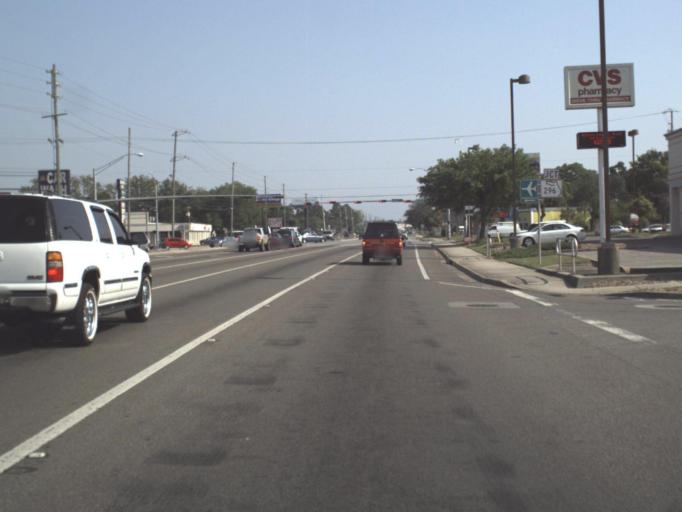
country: US
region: Florida
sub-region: Escambia County
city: Brent
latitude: 30.4678
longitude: -87.2429
